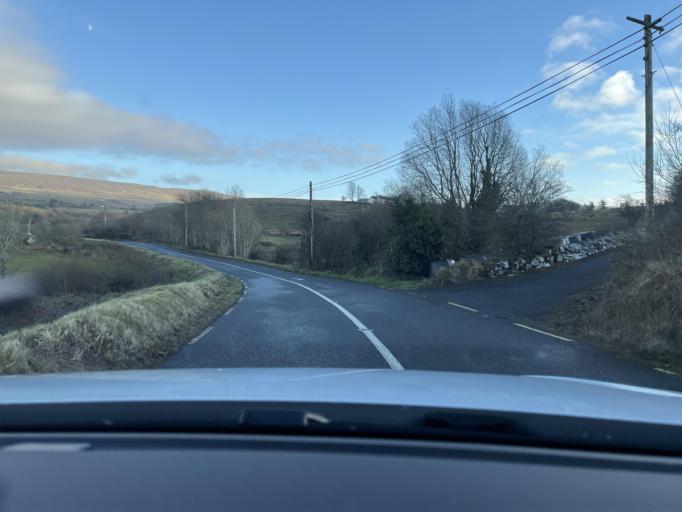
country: IE
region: Connaught
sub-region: County Leitrim
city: Manorhamilton
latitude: 54.1910
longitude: -7.9086
